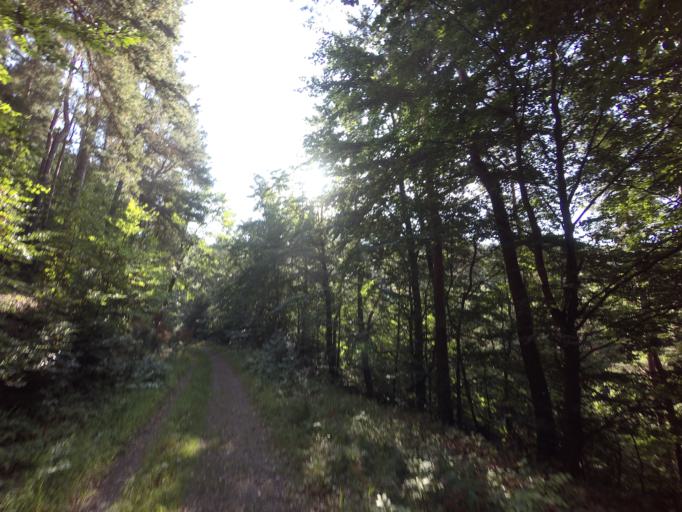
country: DE
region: North Rhine-Westphalia
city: Heimbach
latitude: 50.6146
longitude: 6.4079
